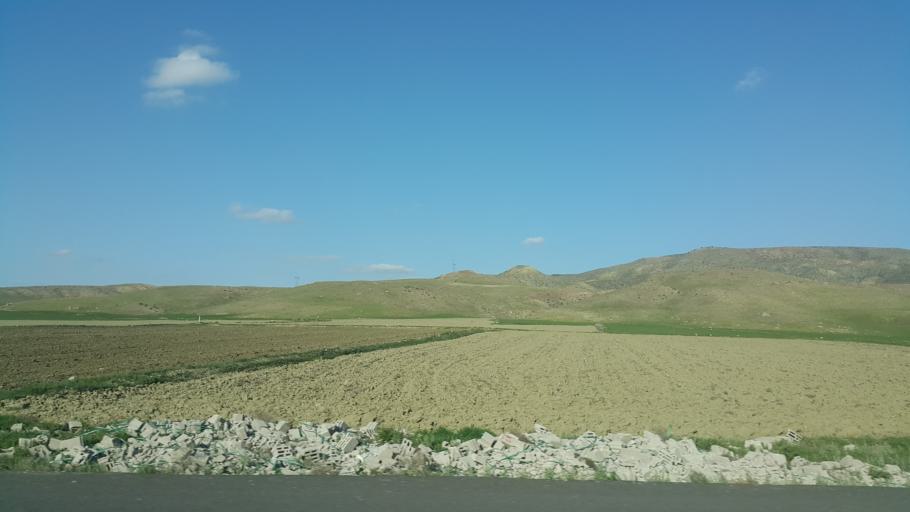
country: TR
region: Ankara
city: Sereflikochisar
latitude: 38.8312
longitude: 33.5945
